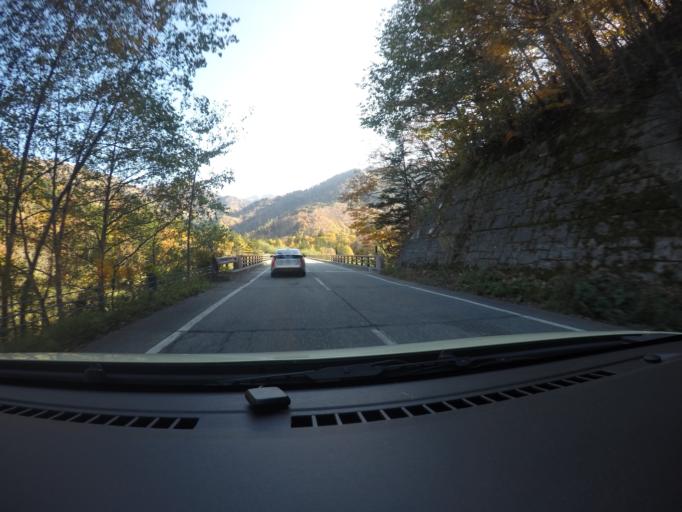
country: JP
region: Gifu
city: Takayama
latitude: 36.1886
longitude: 137.5479
